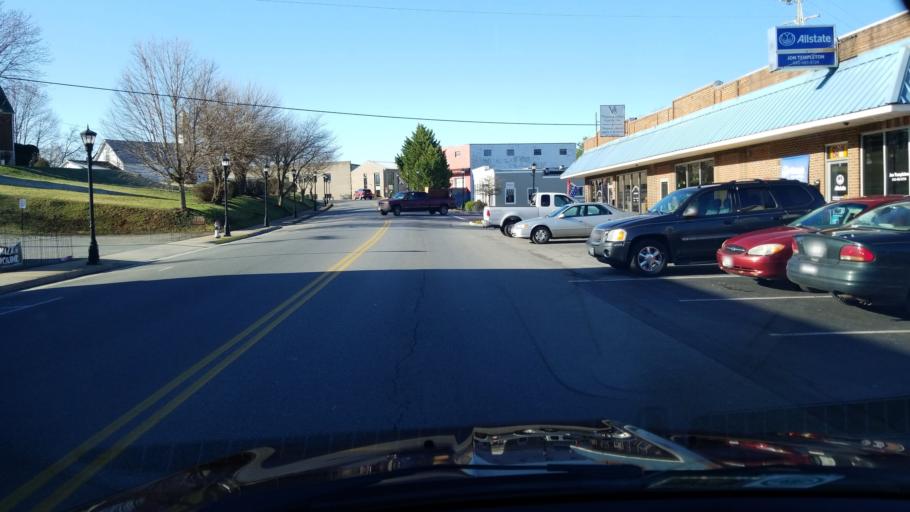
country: US
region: Virginia
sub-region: Franklin County
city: Rocky Mount
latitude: 37.0005
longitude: -79.8926
